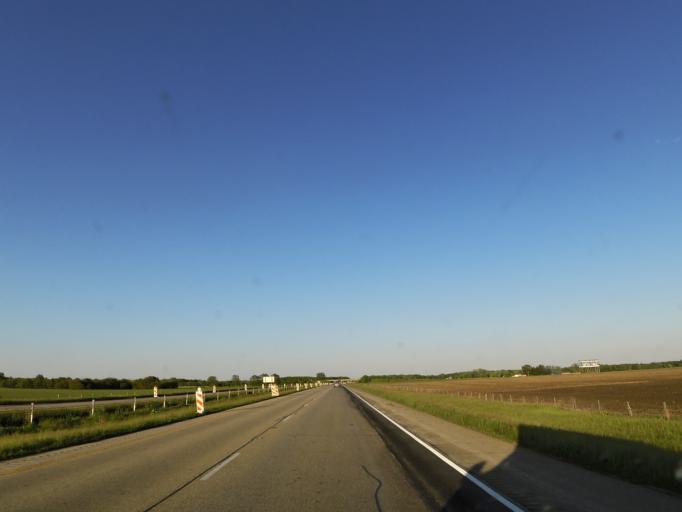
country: US
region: Illinois
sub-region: Vermilion County
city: Oakwood
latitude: 40.1272
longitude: -87.7637
